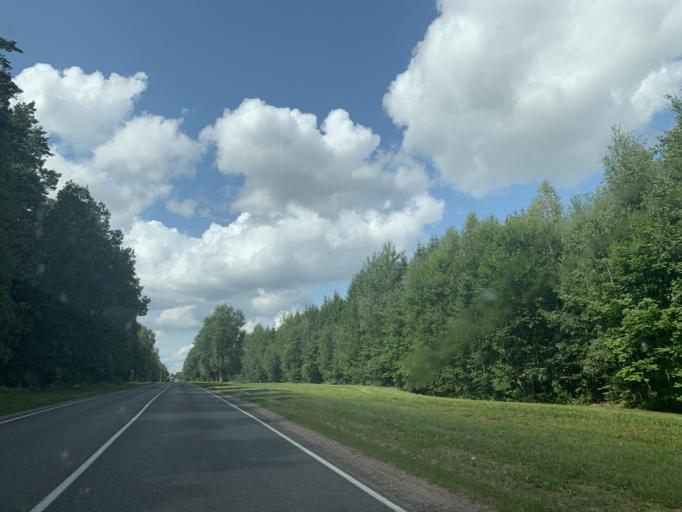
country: BY
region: Minsk
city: Enyerhyetykaw
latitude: 53.5715
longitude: 27.0626
